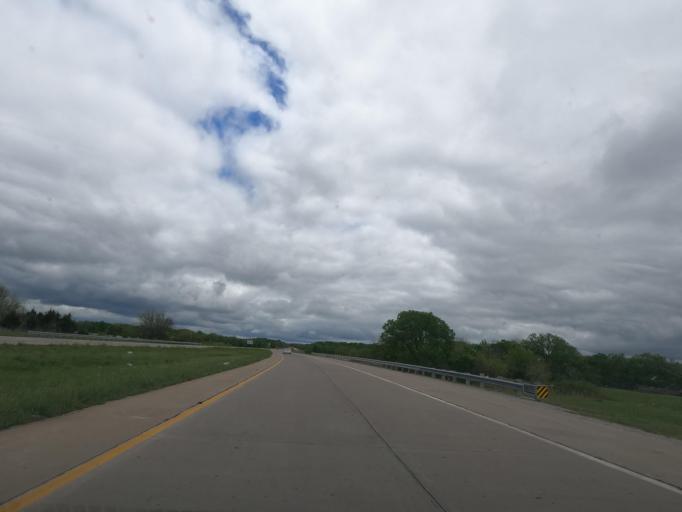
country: US
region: Kansas
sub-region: Wilson County
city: Neodesha
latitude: 37.3573
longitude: -95.6881
